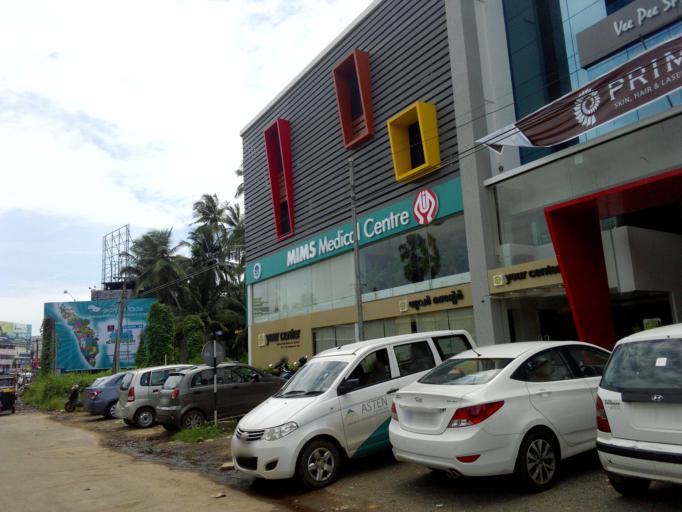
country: IN
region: Kerala
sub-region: Kozhikode
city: Kozhikode
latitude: 11.2810
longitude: 75.7873
